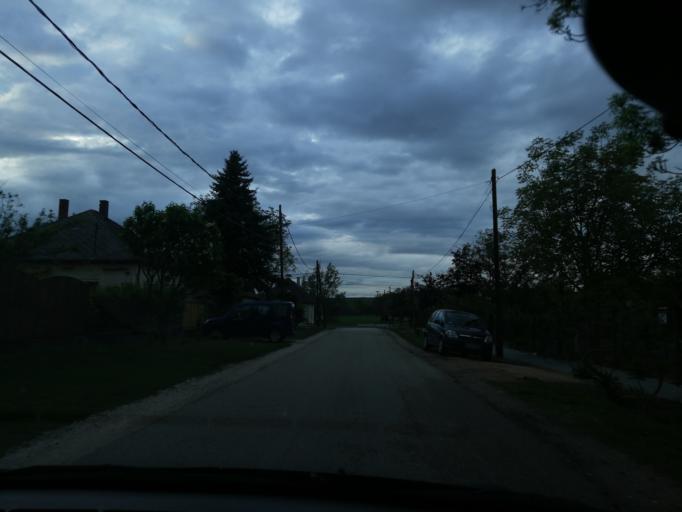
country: HU
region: Fejer
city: Pakozd
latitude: 47.1784
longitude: 18.5662
